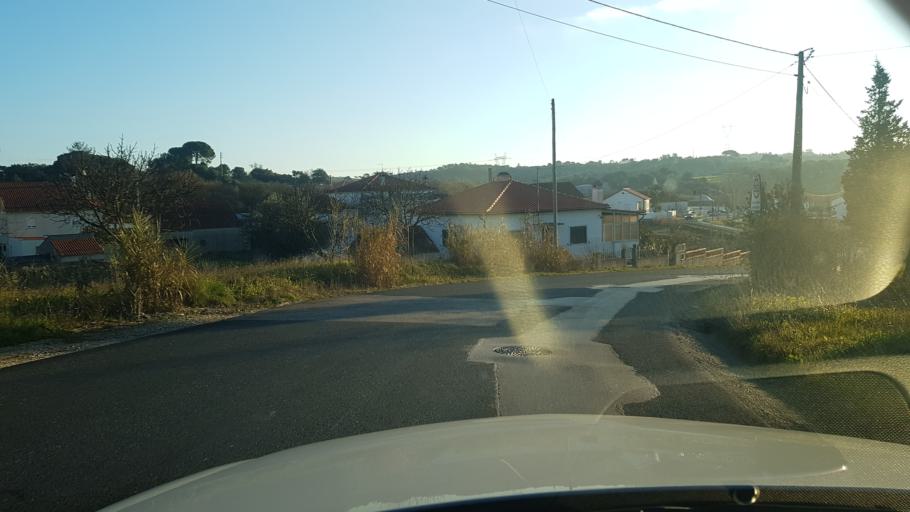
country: PT
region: Santarem
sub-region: Torres Novas
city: Torres Novas
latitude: 39.5534
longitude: -8.5564
